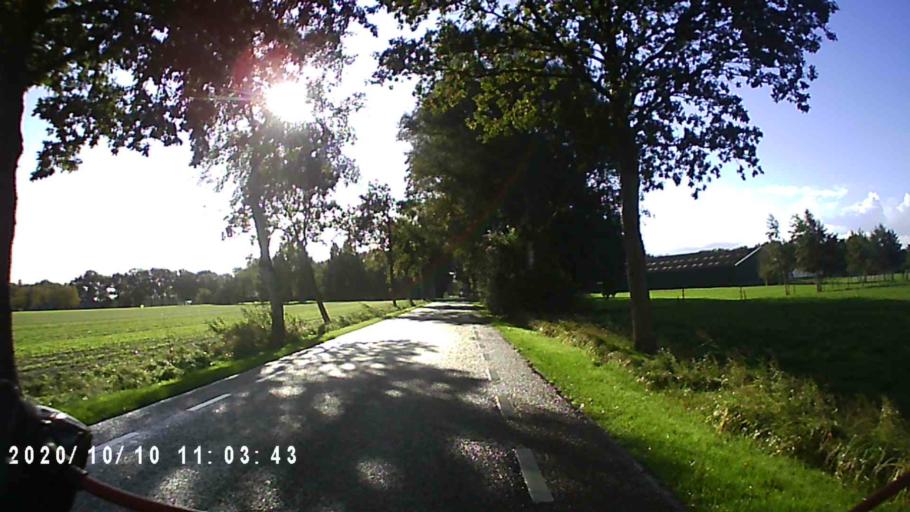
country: NL
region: Friesland
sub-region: Gemeente Achtkarspelen
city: Surhuisterveen
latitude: 53.1335
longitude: 6.2235
